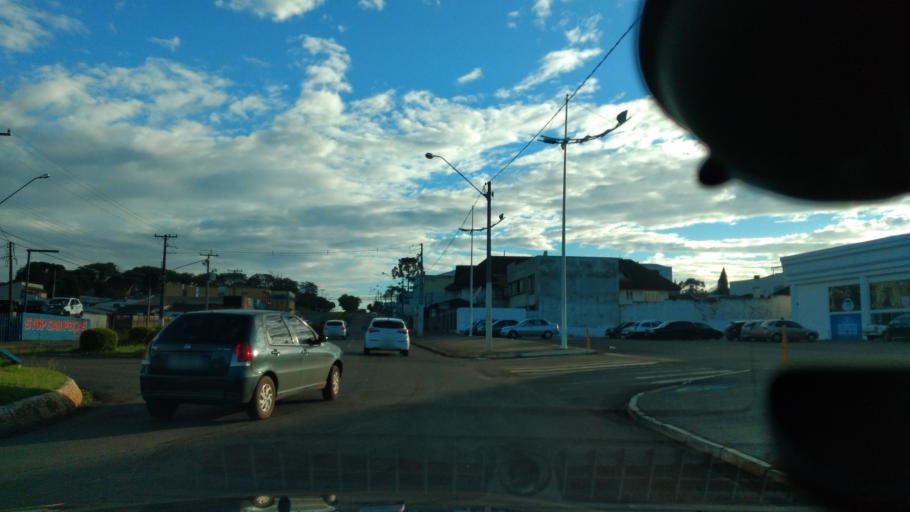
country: BR
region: Parana
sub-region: Guarapuava
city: Guarapuava
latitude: -25.3930
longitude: -51.4805
